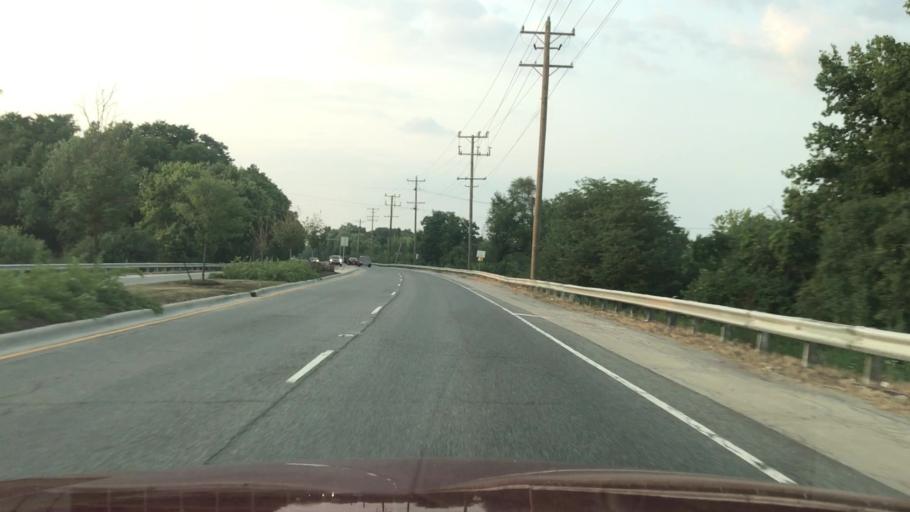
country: US
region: Illinois
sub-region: Will County
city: Lockport
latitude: 41.5953
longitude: -88.0749
